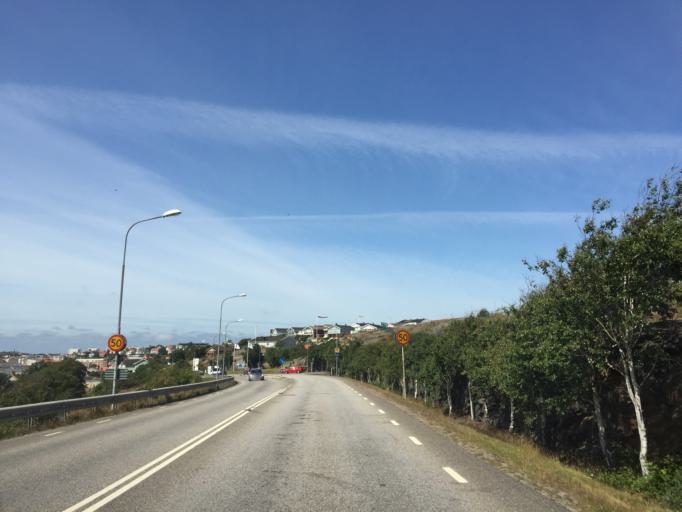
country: SE
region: Vaestra Goetaland
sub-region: Lysekils Kommun
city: Lysekil
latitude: 58.2780
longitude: 11.4572
